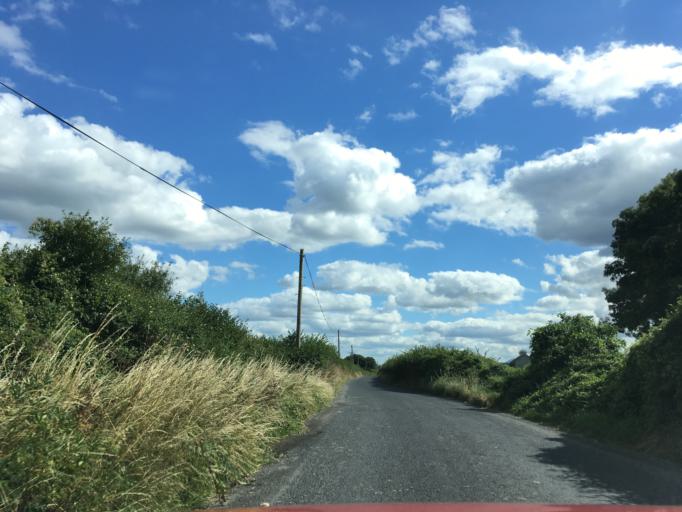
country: IE
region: Munster
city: Cashel
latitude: 52.4678
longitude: -7.9770
